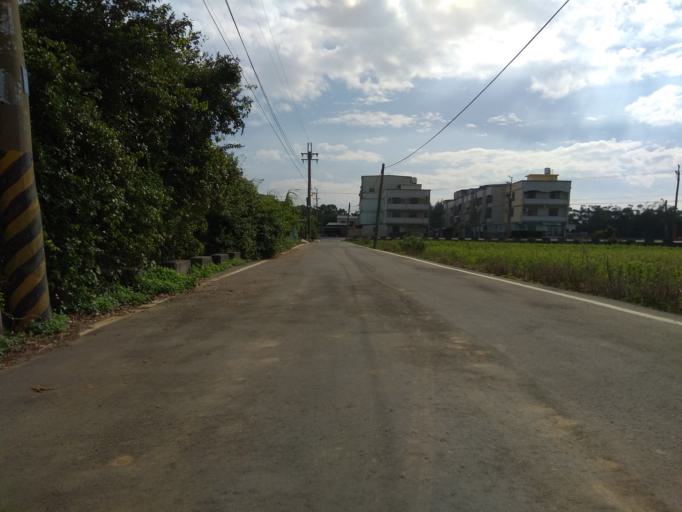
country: TW
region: Taiwan
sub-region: Hsinchu
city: Zhubei
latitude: 24.9490
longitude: 121.0064
